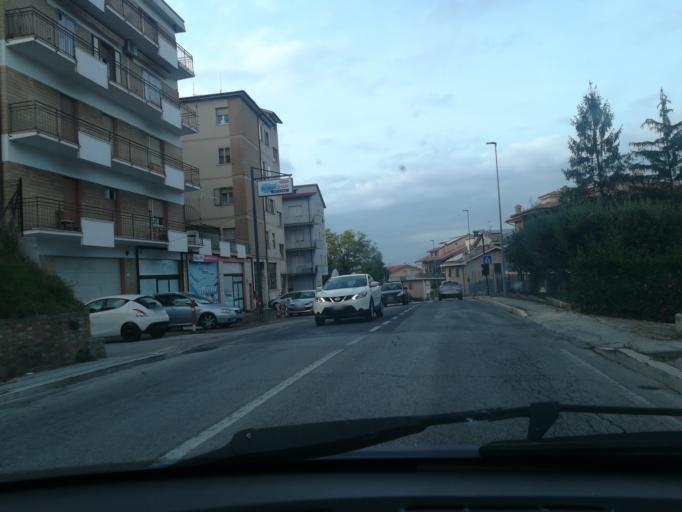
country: IT
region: The Marches
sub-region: Provincia di Macerata
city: Villa Potenza
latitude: 43.3080
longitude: 13.4378
